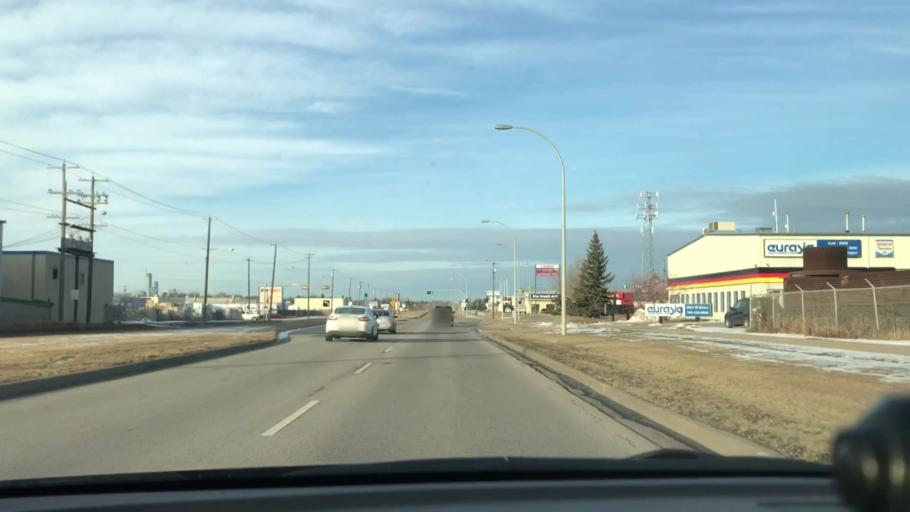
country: CA
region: Alberta
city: Edmonton
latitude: 53.4925
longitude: -113.4670
